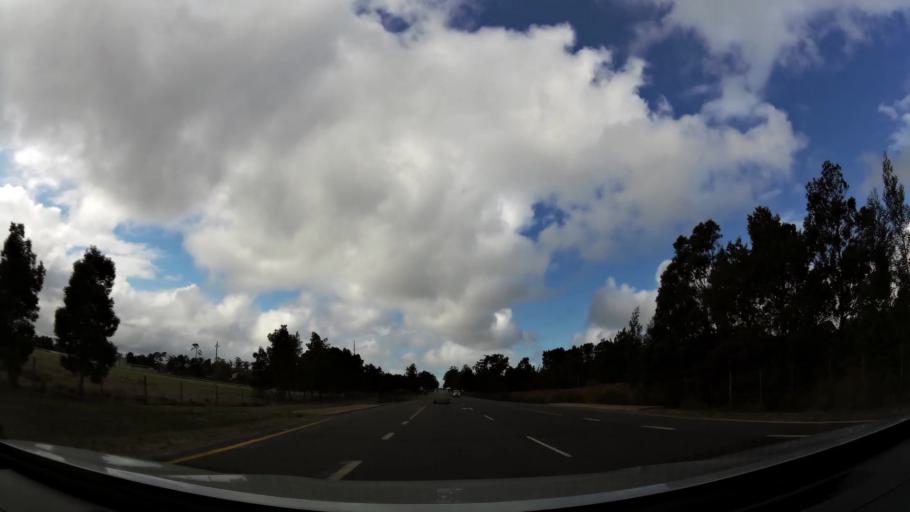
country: ZA
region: Western Cape
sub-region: Eden District Municipality
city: Plettenberg Bay
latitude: -34.0443
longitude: 23.2804
